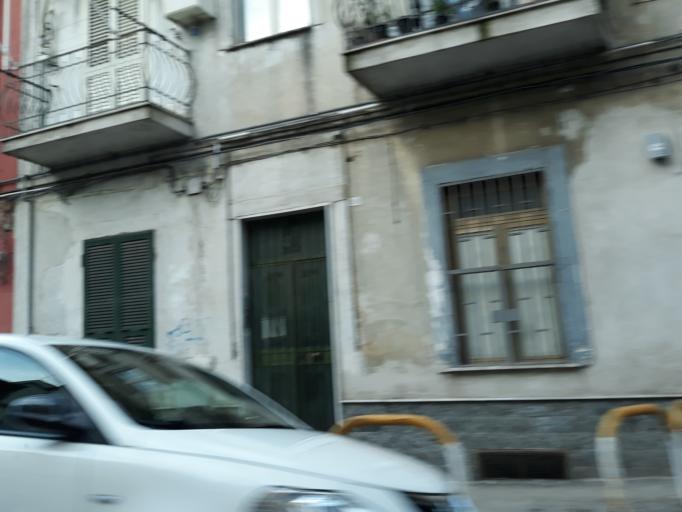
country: IT
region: Campania
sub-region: Provincia di Napoli
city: Mugnano di Napoli
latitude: 40.8852
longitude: 14.2291
